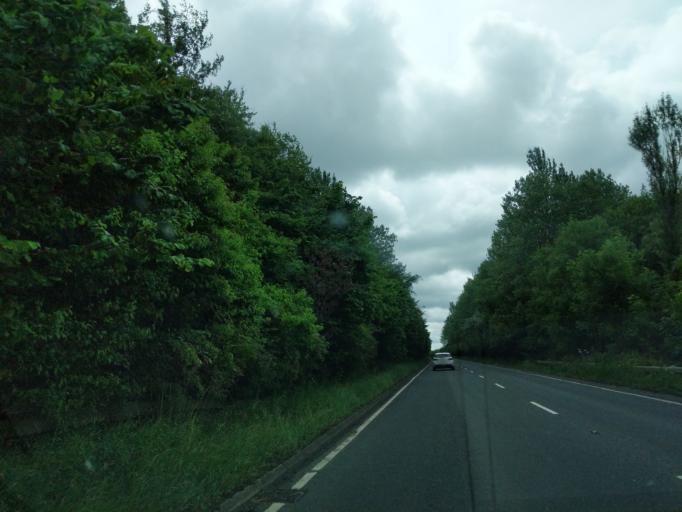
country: GB
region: Scotland
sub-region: South Lanarkshire
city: Stonehouse
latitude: 55.7007
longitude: -3.9847
